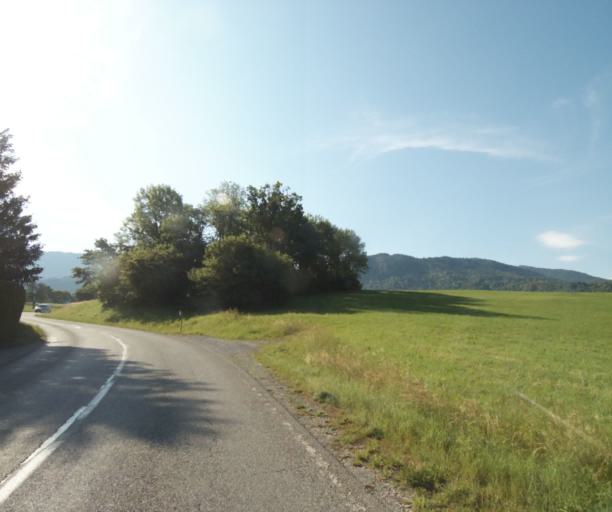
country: FR
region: Rhone-Alpes
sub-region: Departement de la Haute-Savoie
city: Allinges
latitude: 46.3194
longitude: 6.4764
